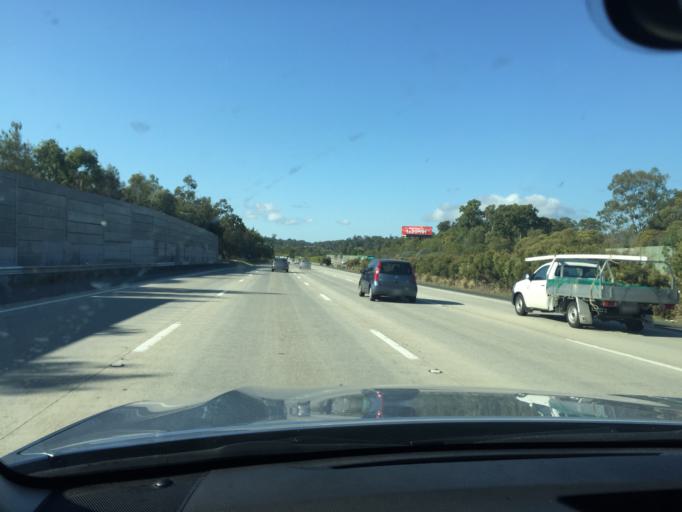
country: AU
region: Queensland
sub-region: Gold Coast
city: Ormeau Hills
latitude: -27.7931
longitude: 153.2601
